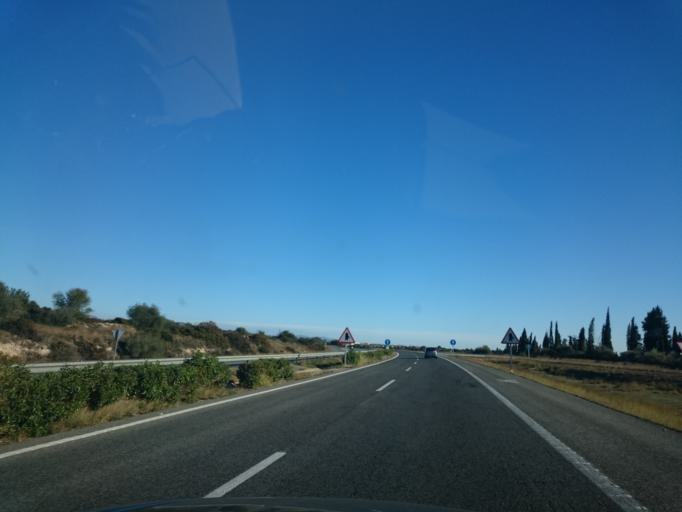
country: ES
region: Catalonia
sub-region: Provincia de Tarragona
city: Amposta
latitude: 40.7327
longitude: 0.5860
